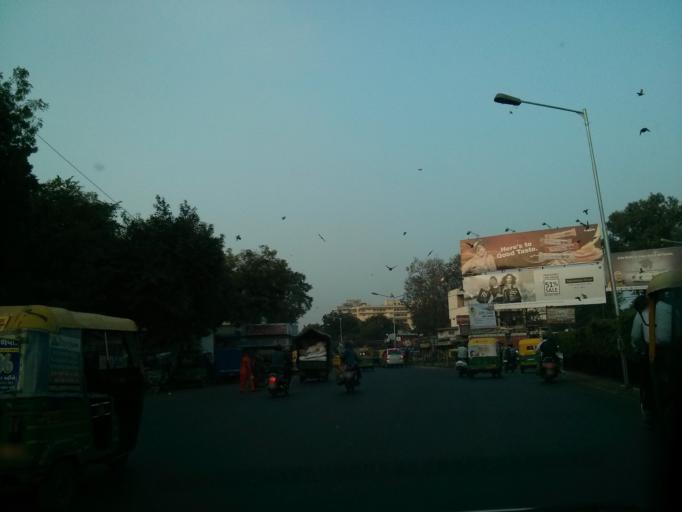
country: IN
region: Gujarat
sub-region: Ahmadabad
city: Ahmedabad
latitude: 23.0430
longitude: 72.5894
